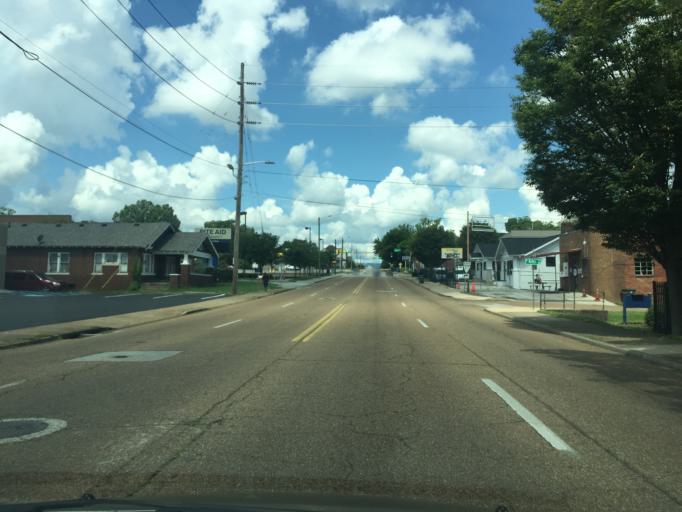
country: US
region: Tennessee
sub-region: Hamilton County
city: East Ridge
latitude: 35.0342
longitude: -85.2702
